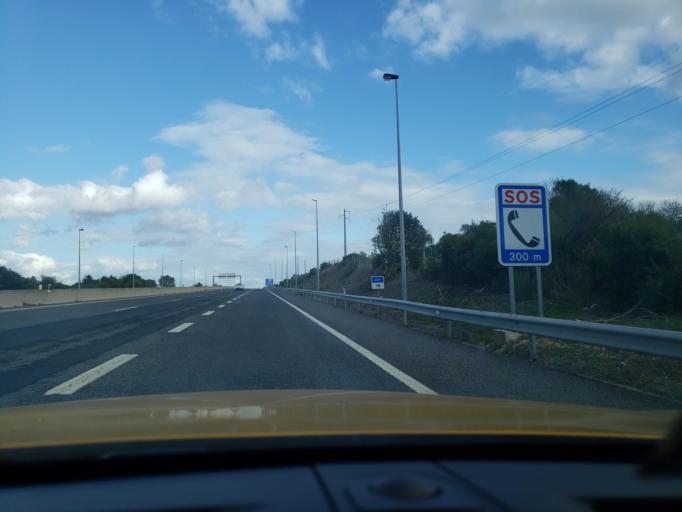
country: PT
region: Faro
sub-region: Portimao
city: Portimao
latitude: 37.1763
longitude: -8.5652
